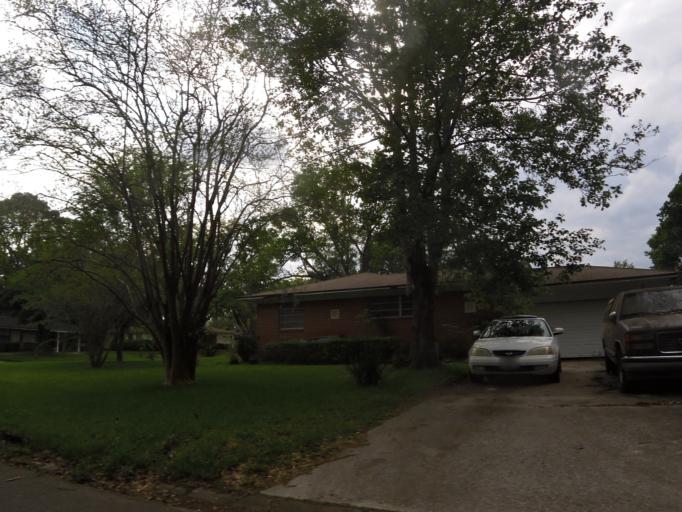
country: US
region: Florida
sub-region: Duval County
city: Jacksonville
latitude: 30.2939
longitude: -81.7352
